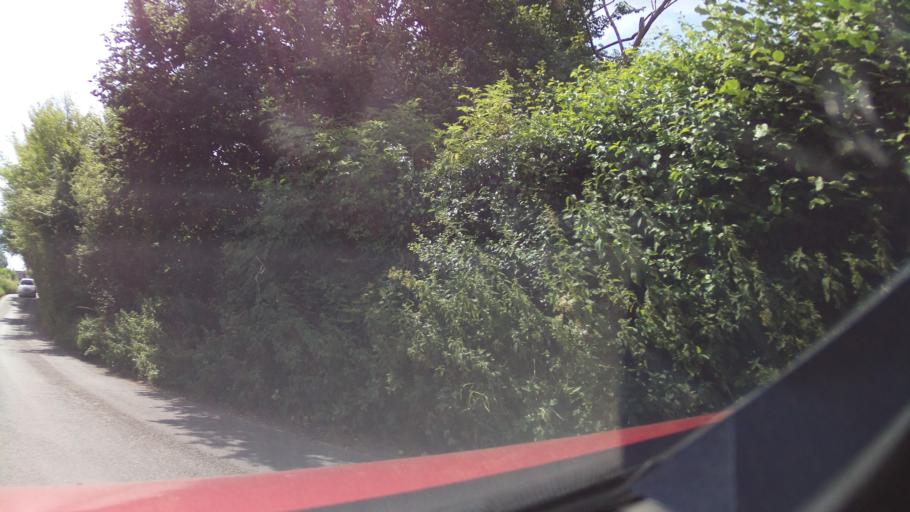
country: GB
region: England
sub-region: Wiltshire
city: Purton
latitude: 51.5756
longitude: -1.8654
